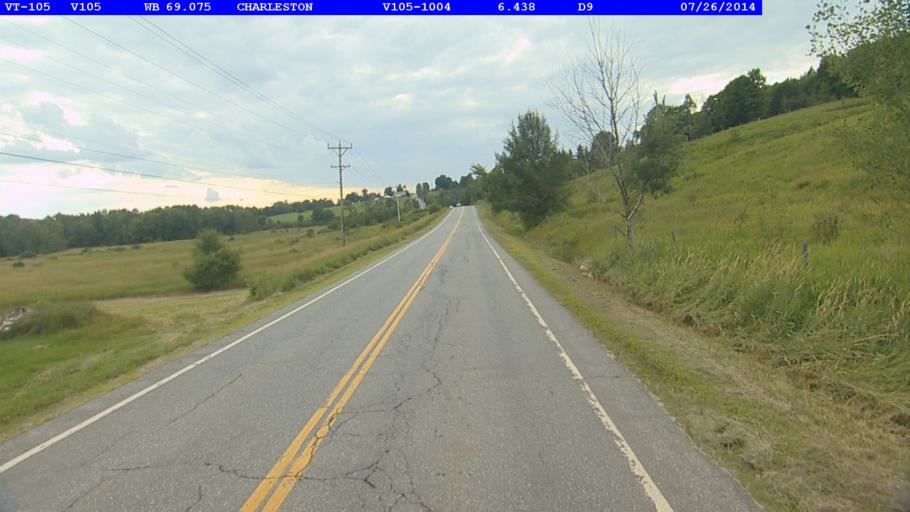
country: US
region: Vermont
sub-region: Orleans County
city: Newport
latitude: 44.8412
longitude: -72.0014
